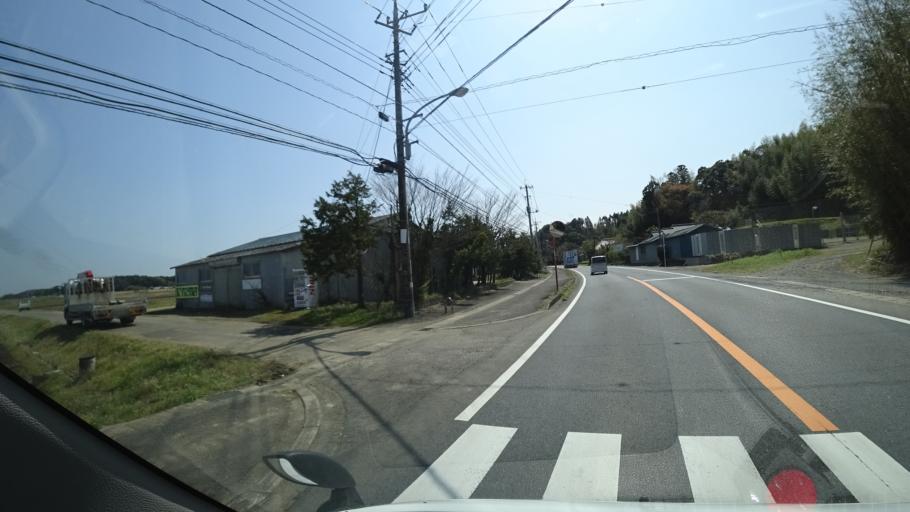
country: JP
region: Chiba
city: Narita
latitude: 35.8142
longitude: 140.3076
